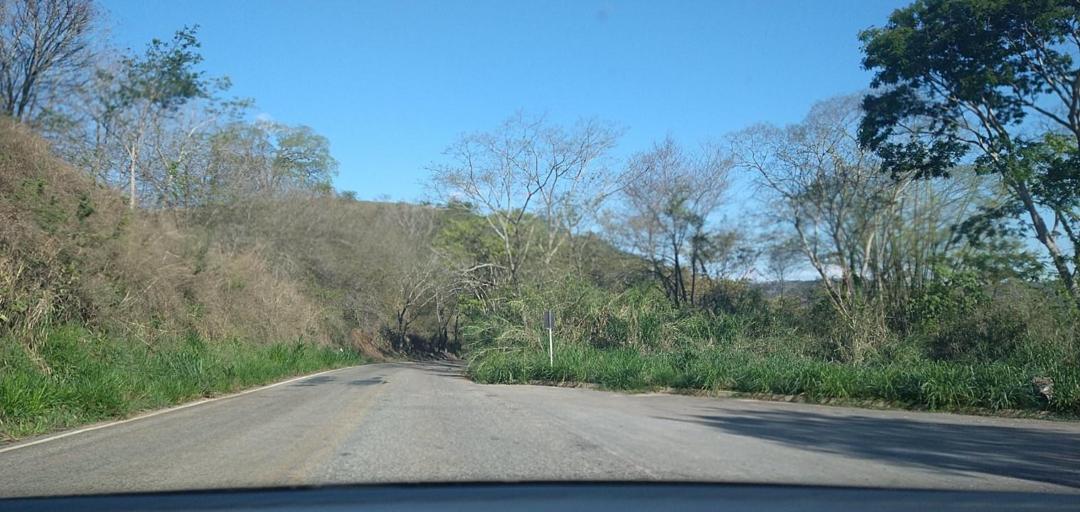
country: BR
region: Minas Gerais
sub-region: Ponte Nova
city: Ponte Nova
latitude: -20.2411
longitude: -42.8963
